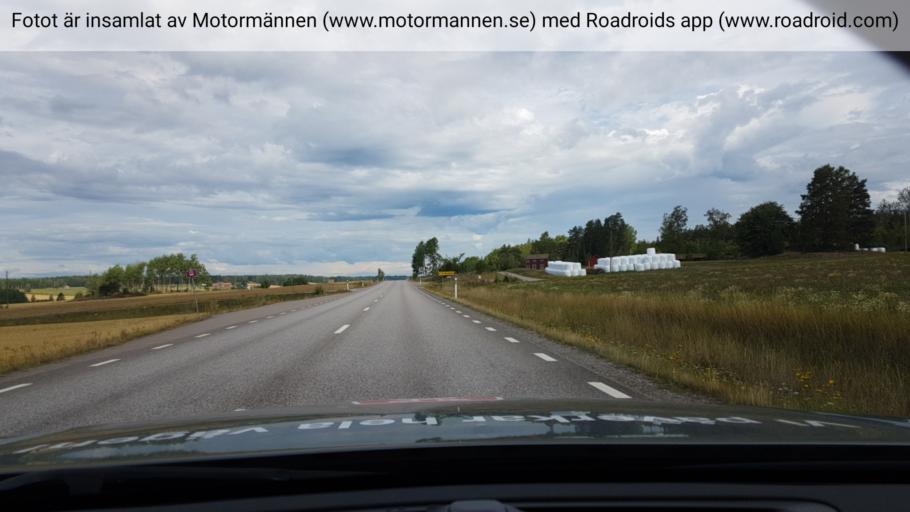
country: SE
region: Uppsala
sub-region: Heby Kommun
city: Morgongava
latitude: 59.8849
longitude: 16.9141
